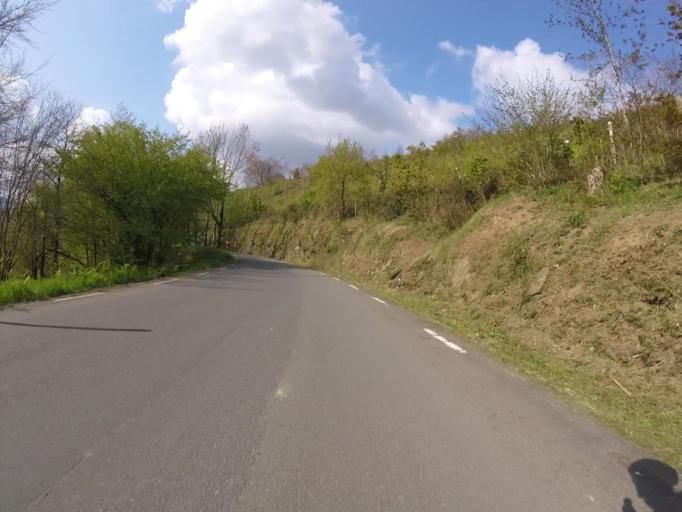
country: ES
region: Basque Country
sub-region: Provincia de Guipuzcoa
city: Azkoitia
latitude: 43.2076
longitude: -2.3495
